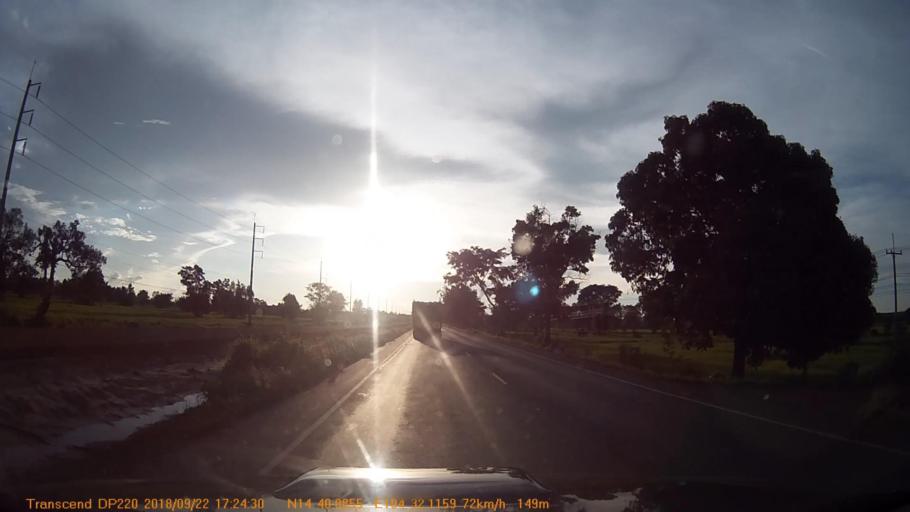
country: TH
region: Sisaket
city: Kantharalak
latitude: 14.6815
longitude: 104.5349
